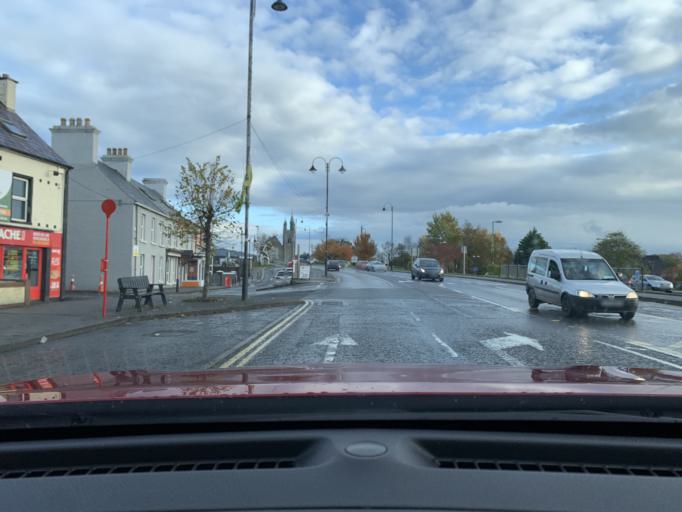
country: IE
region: Ulster
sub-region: County Donegal
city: Ballybofey
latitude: 54.8001
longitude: -7.7786
